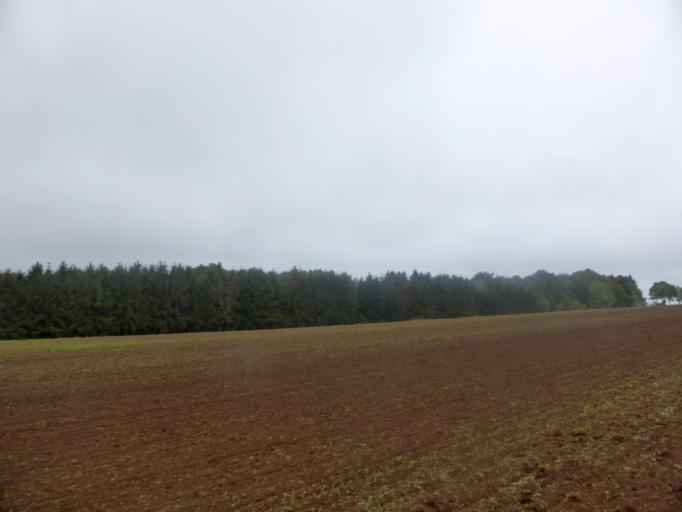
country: LU
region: Diekirch
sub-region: Canton de Wiltz
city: Boulaide
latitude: 49.8612
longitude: 5.7786
